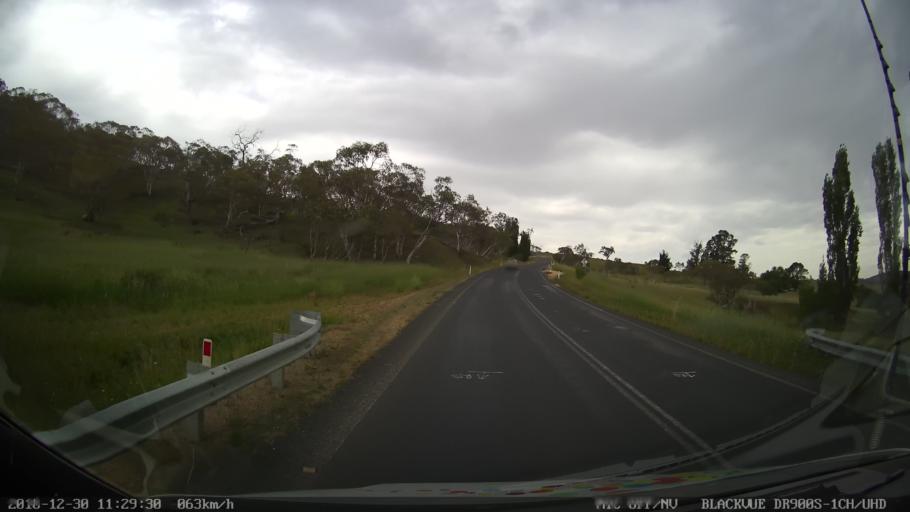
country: AU
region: New South Wales
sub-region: Snowy River
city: Jindabyne
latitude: -36.4500
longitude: 148.6098
